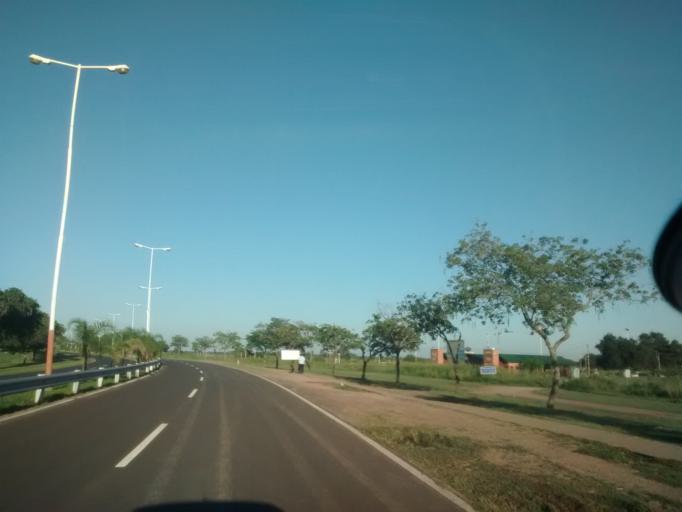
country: AR
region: Chaco
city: Fontana
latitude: -27.4405
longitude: -59.0313
